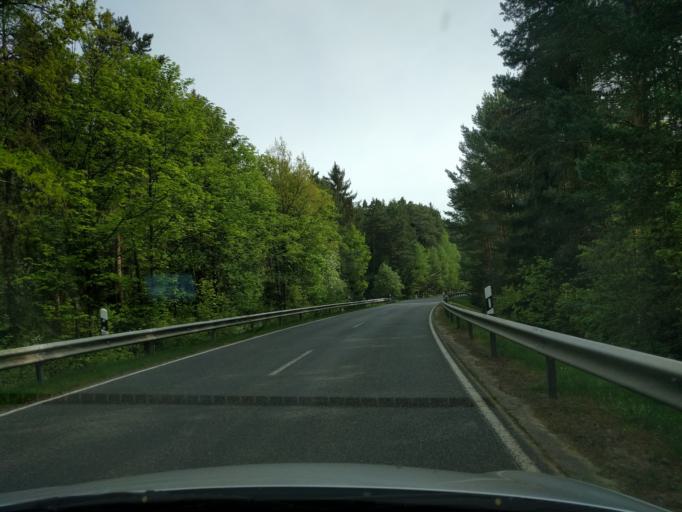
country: DE
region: Bavaria
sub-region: Upper Palatinate
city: Michelsneukirchen
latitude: 49.1434
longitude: 12.5597
